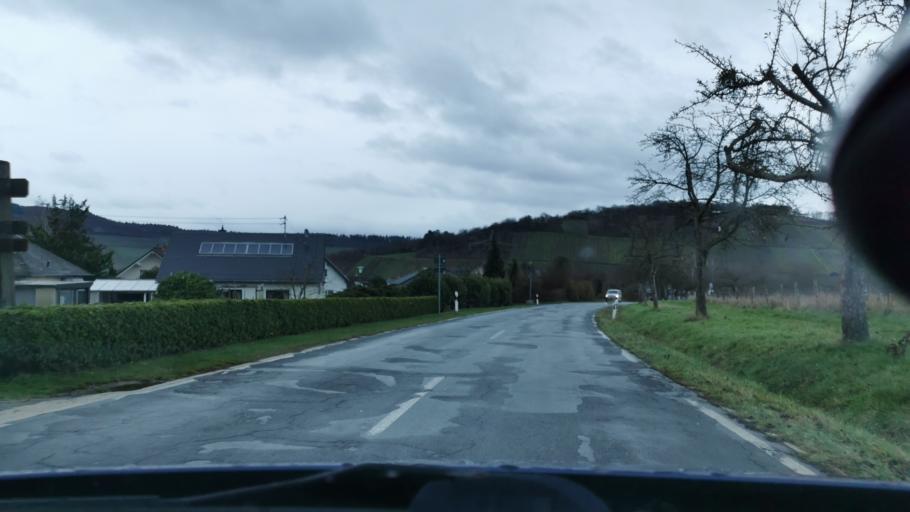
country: DE
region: Rheinland-Pfalz
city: Maring-Noviand
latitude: 49.9278
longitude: 6.9907
